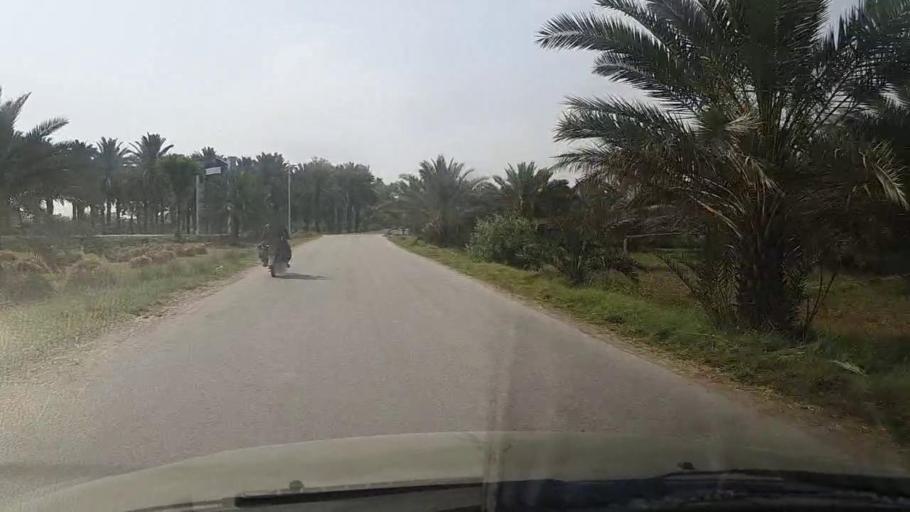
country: PK
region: Sindh
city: Gambat
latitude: 27.4555
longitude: 68.4855
